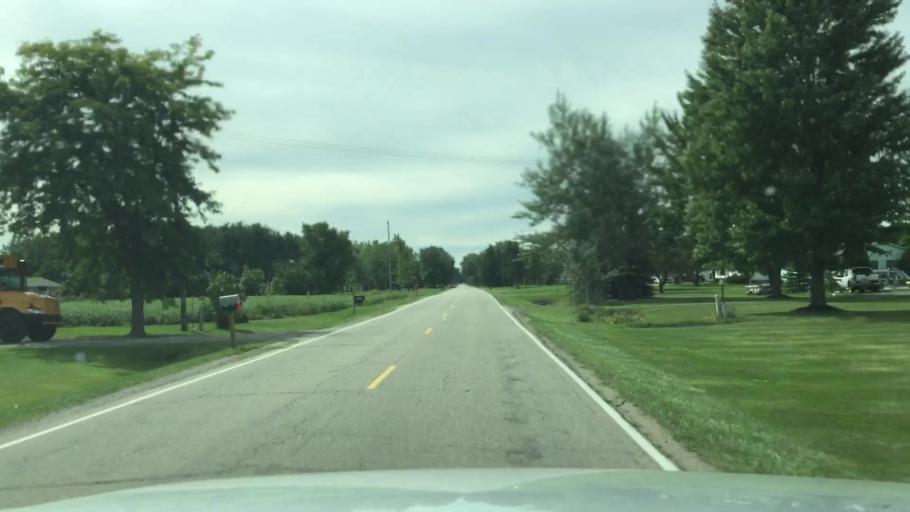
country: US
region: Michigan
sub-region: Genesee County
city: Montrose
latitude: 43.1107
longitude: -83.9880
